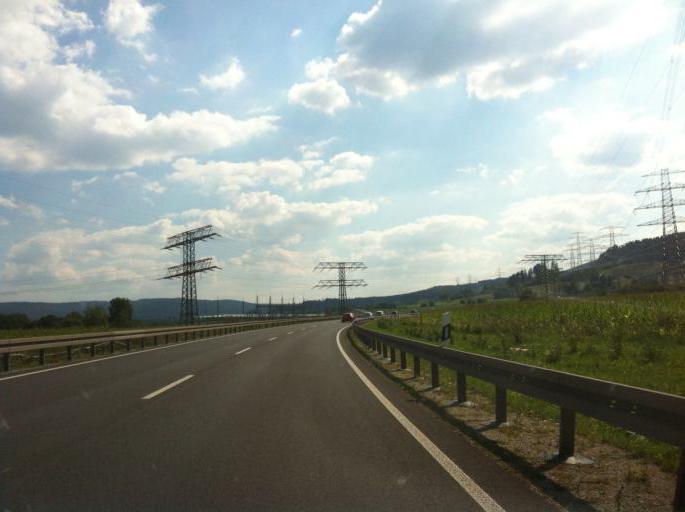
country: DE
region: Thuringia
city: Langewiesen
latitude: 50.6696
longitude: 10.9905
